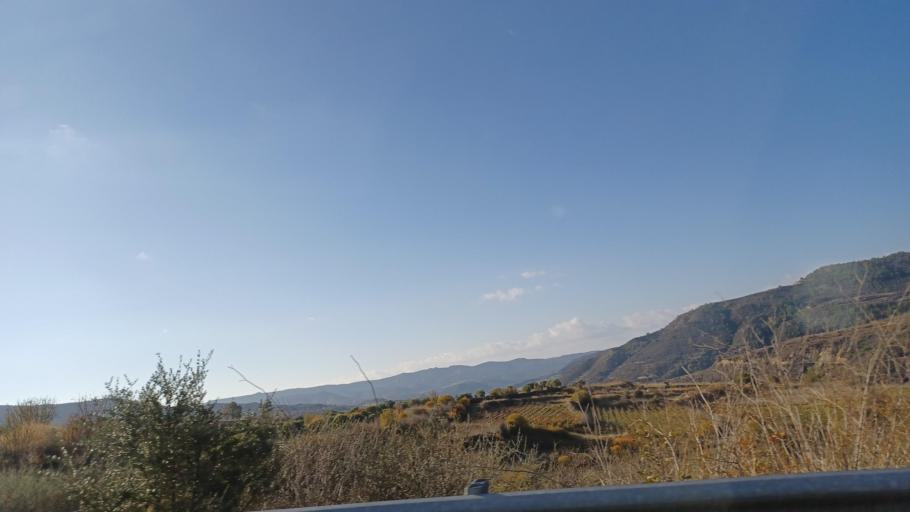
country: CY
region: Limassol
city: Pachna
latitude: 34.8492
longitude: 32.7296
